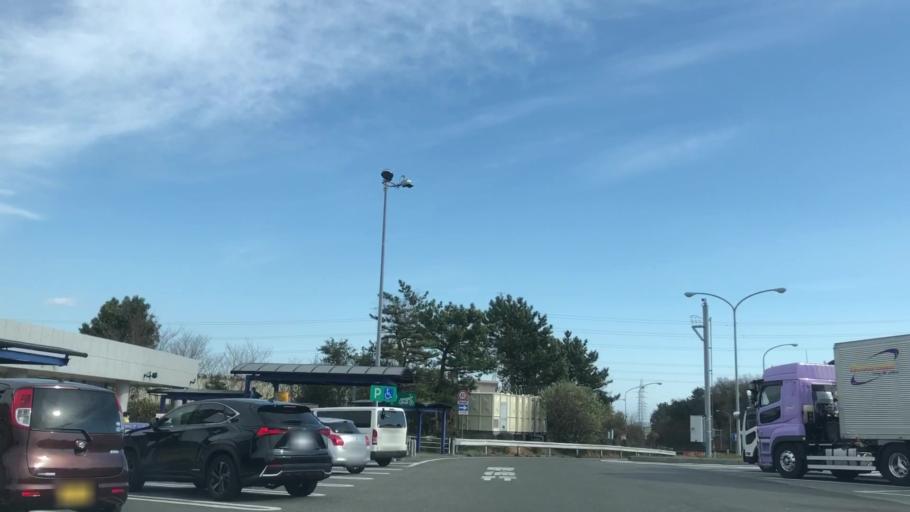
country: JP
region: Shizuoka
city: Hamamatsu
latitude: 34.7575
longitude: 137.7383
